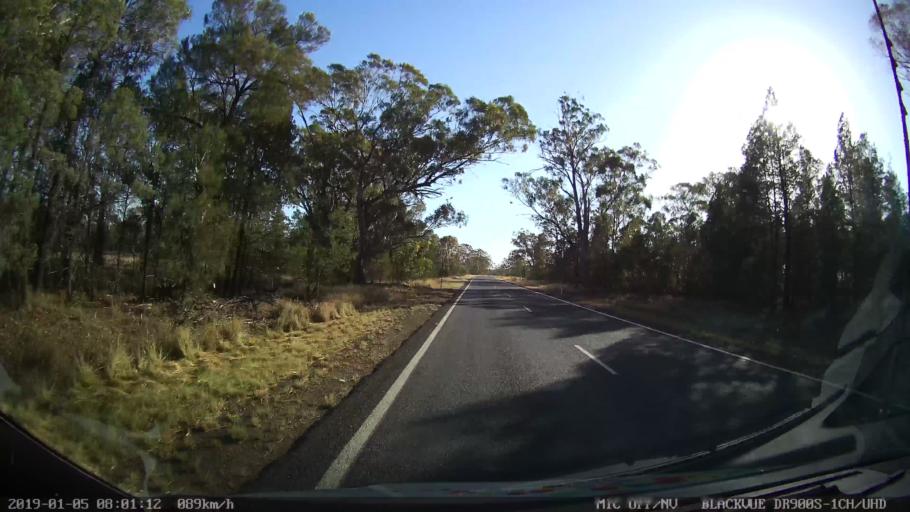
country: AU
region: New South Wales
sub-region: Gilgandra
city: Gilgandra
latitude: -31.6881
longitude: 148.6992
